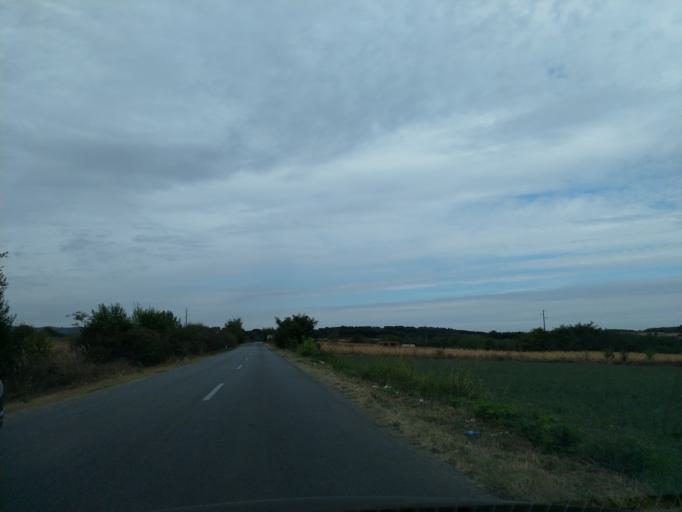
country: RS
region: Central Serbia
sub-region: Pomoravski Okrug
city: Jagodina
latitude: 43.9991
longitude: 21.2162
